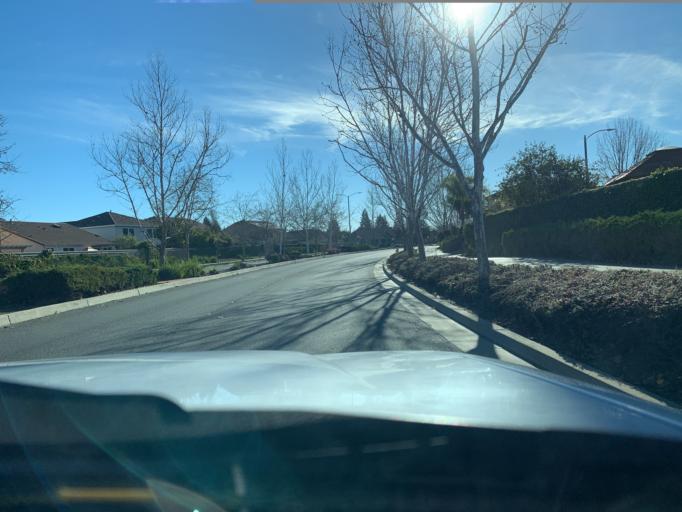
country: US
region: California
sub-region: Yolo County
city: Woodland
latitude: 38.6716
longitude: -121.7432
